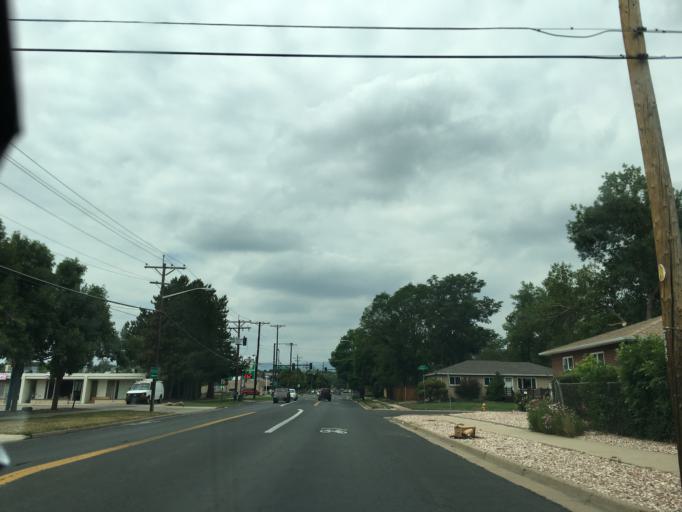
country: US
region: Colorado
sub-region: Arapahoe County
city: Sheridan
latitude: 39.6574
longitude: -105.0483
